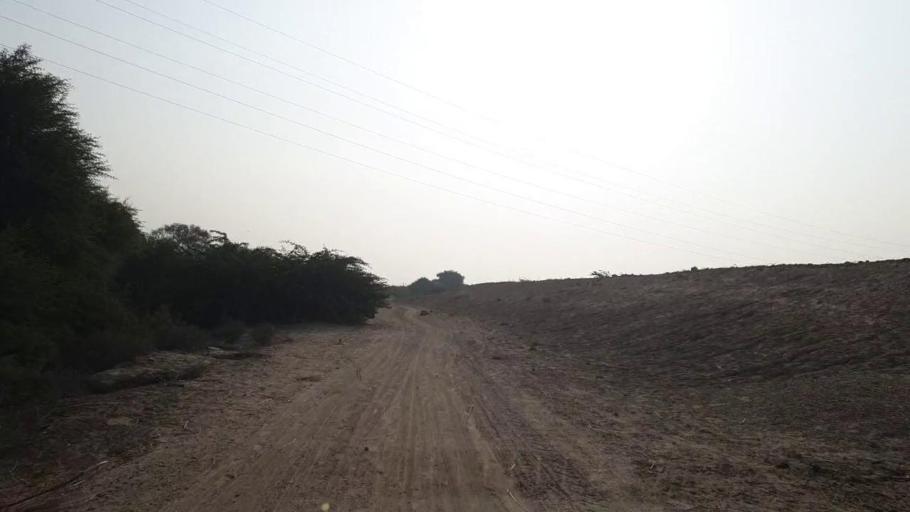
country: PK
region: Sindh
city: Tando Muhammad Khan
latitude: 25.1069
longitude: 68.3024
